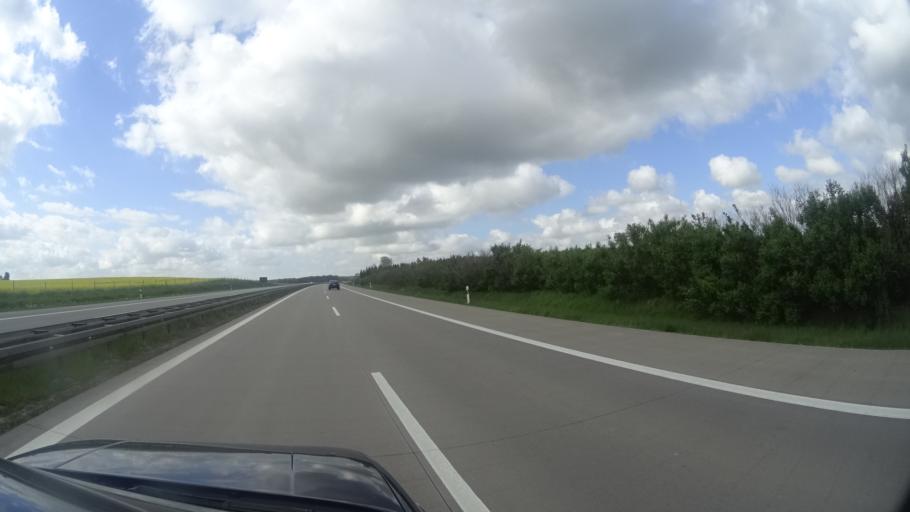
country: DE
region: Mecklenburg-Vorpommern
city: Dummerstorf
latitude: 53.9101
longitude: 12.2411
